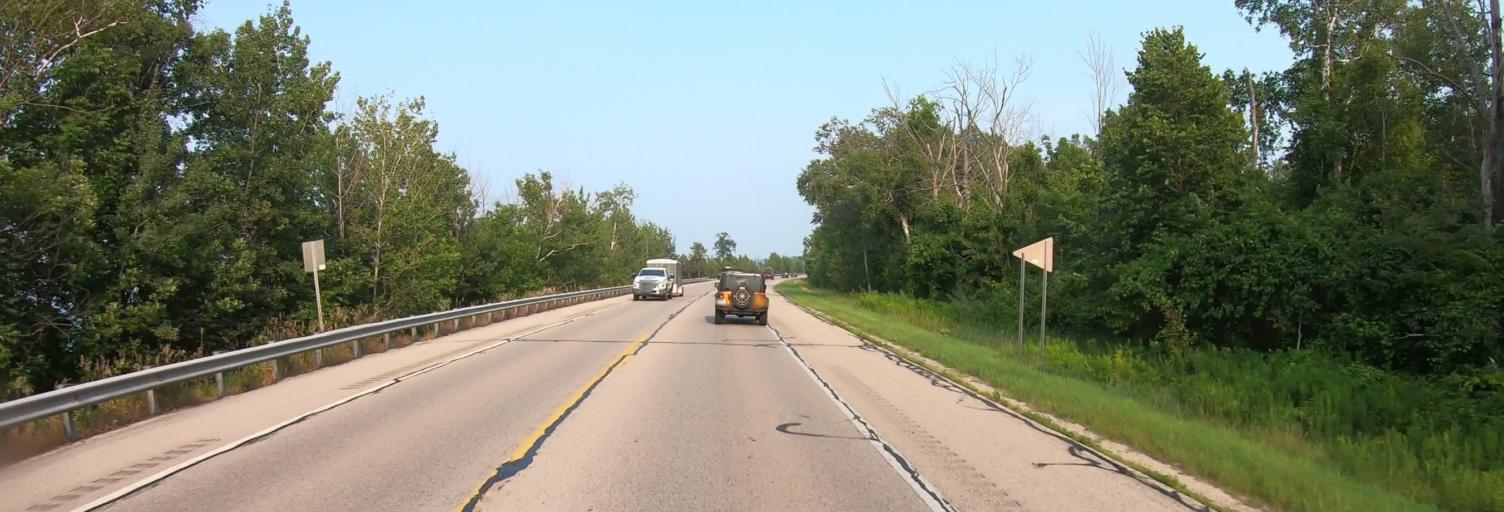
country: US
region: Michigan
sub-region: Charlevoix County
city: Charlevoix
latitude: 45.3686
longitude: -85.1325
